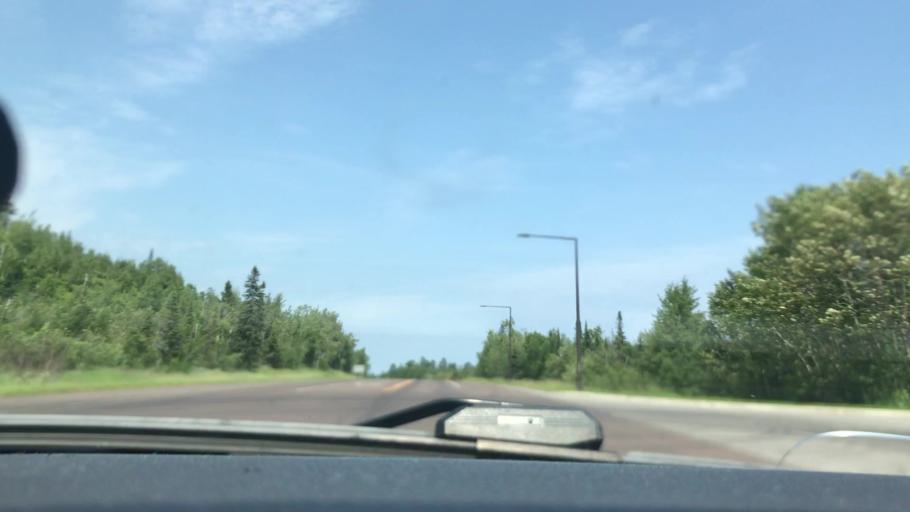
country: US
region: Minnesota
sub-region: Lake County
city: Silver Bay
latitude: 47.3397
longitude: -91.1966
